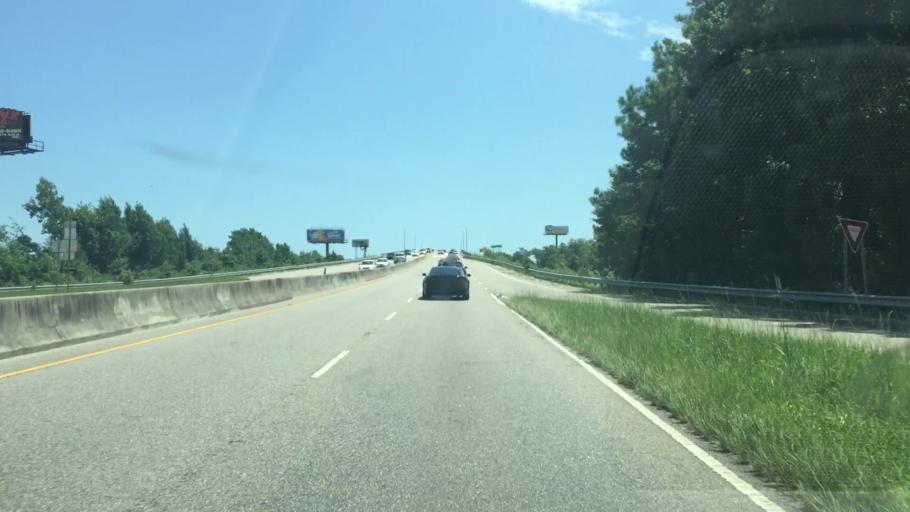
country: US
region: South Carolina
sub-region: Horry County
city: Little River
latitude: 33.8573
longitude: -78.6560
